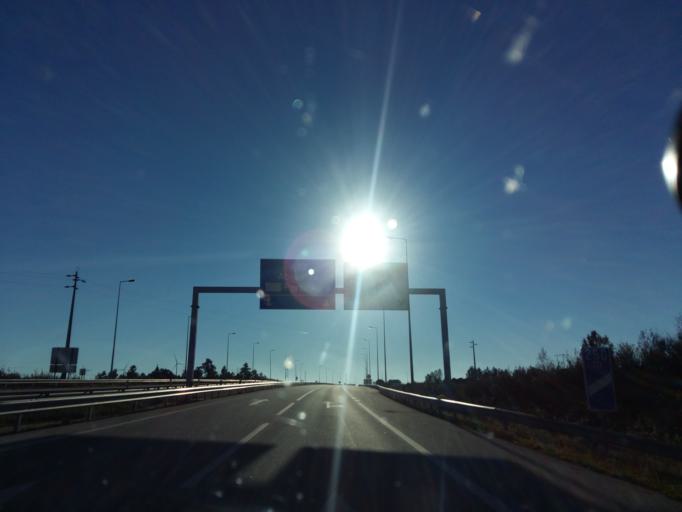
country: PT
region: Castelo Branco
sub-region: Castelo Branco
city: Castelo Branco
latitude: 39.7896
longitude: -7.5663
